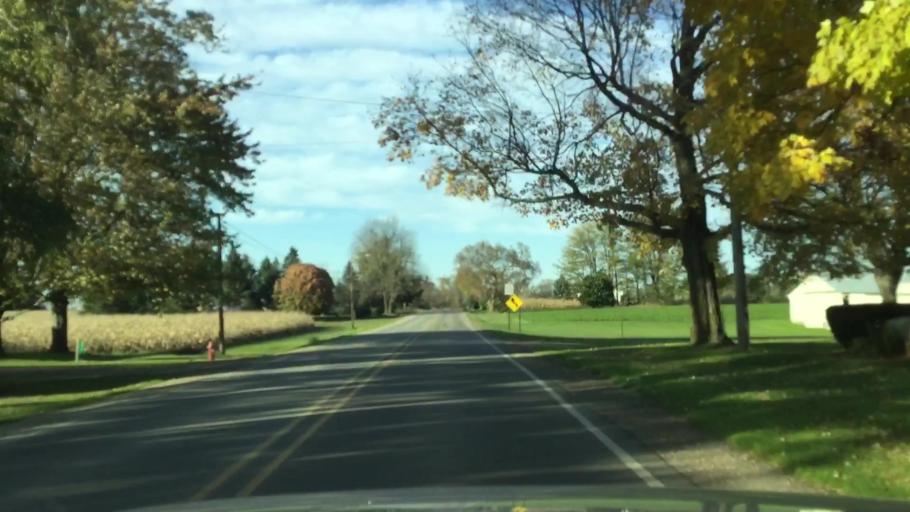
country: US
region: Michigan
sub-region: Lapeer County
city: North Branch
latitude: 43.2345
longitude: -83.1960
